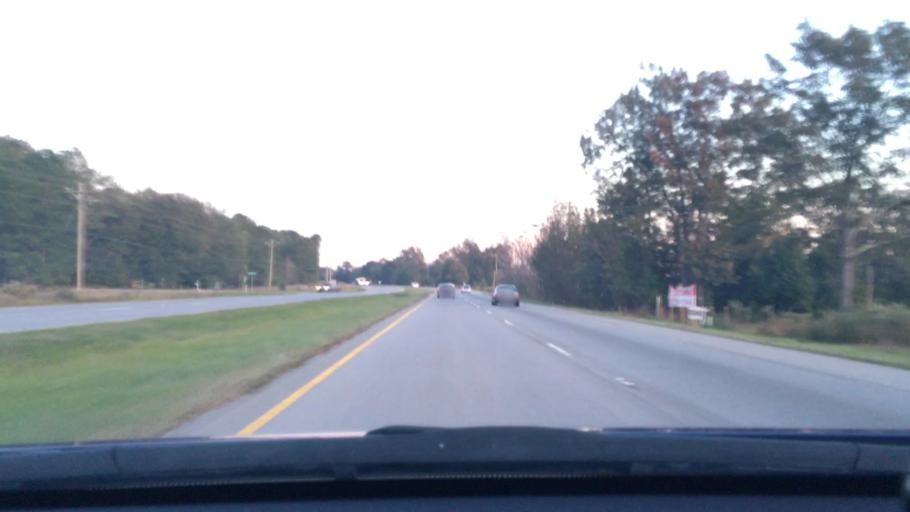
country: US
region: South Carolina
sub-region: Richland County
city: Gadsden
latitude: 33.9400
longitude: -80.7163
